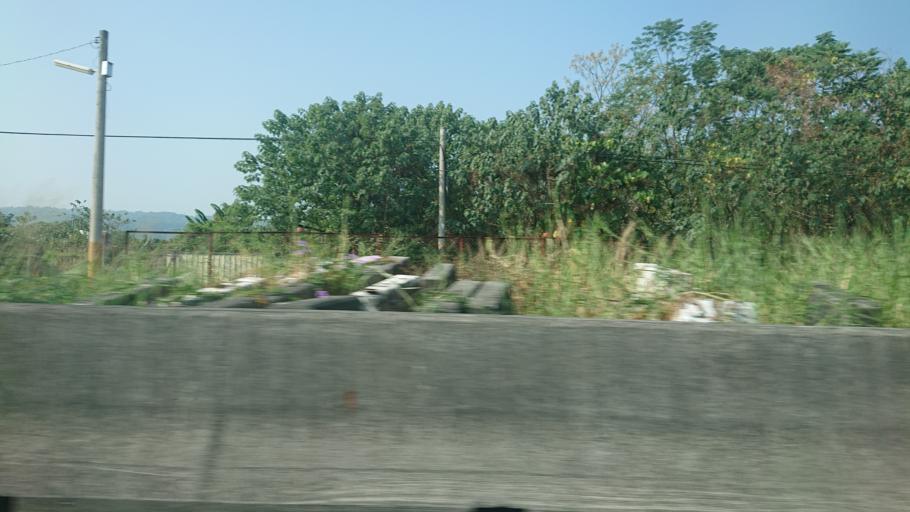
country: TW
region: Taiwan
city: Lugu
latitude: 23.7694
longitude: 120.6594
